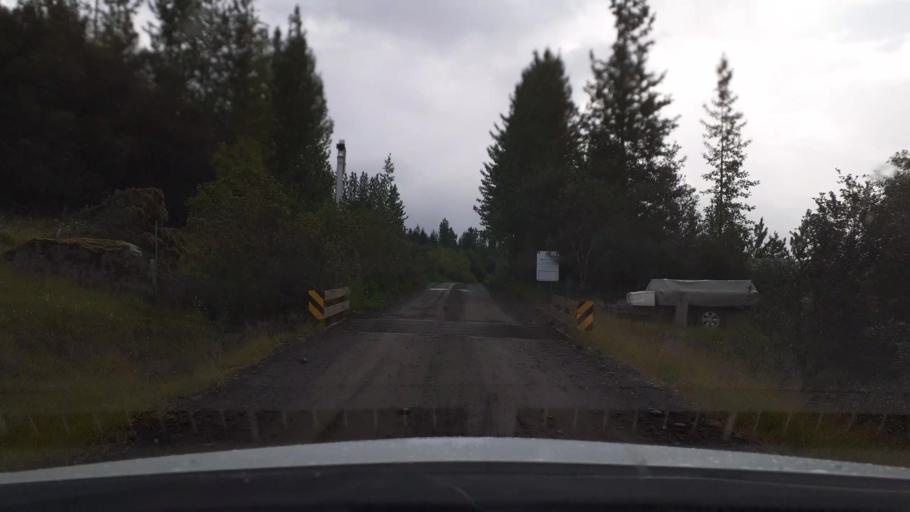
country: IS
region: Capital Region
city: Mosfellsbaer
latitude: 64.4974
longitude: -21.3584
